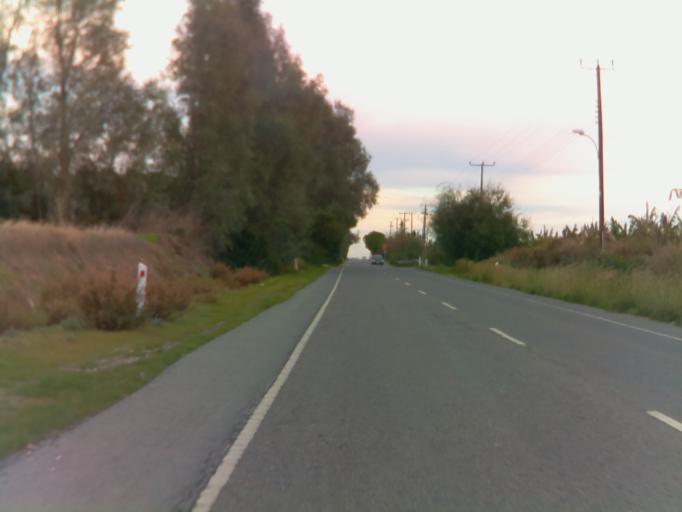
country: CY
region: Pafos
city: Pegeia
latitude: 34.8648
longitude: 32.3692
